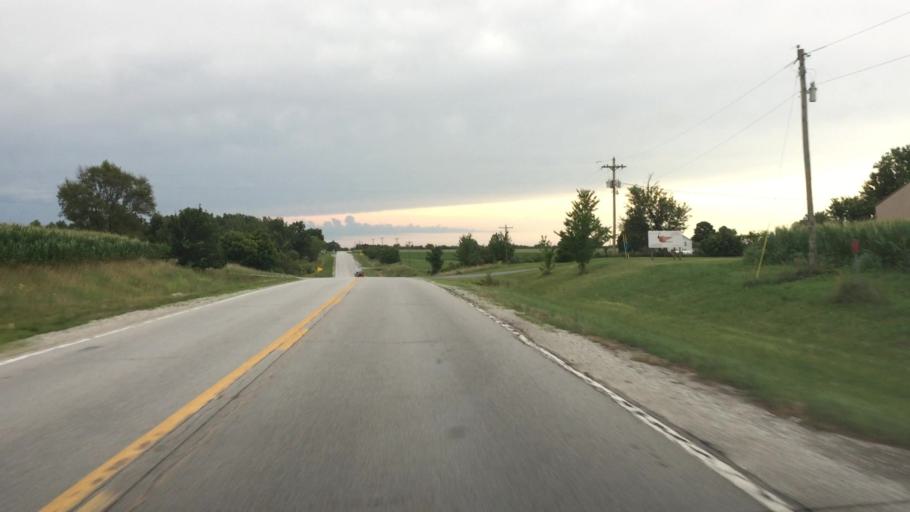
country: US
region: Illinois
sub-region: Hancock County
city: Hamilton
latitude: 40.3761
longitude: -91.3422
